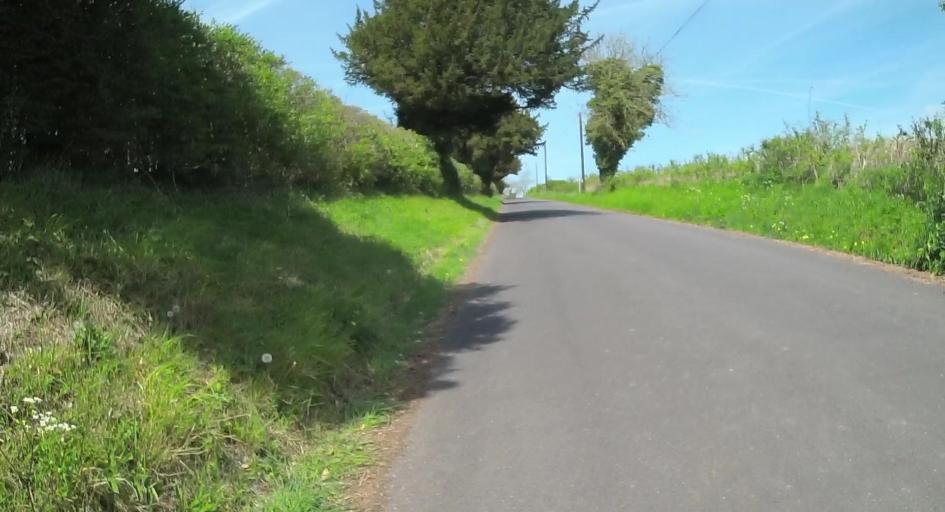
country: GB
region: England
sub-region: Hampshire
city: Romsey
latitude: 51.0800
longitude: -1.4872
